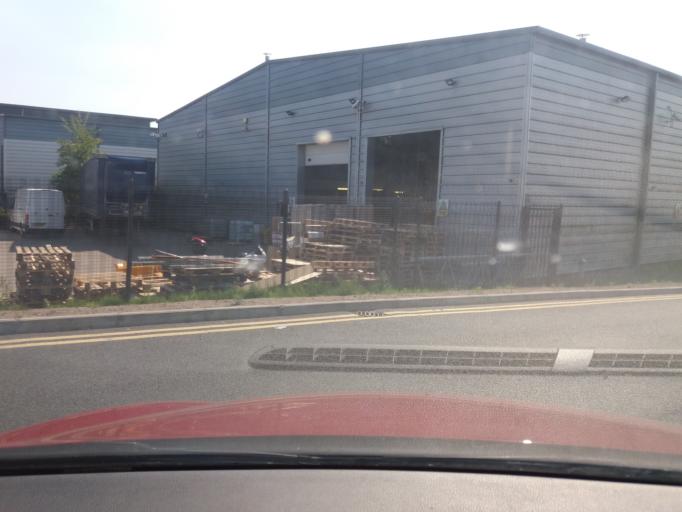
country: GB
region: England
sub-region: Lancashire
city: Clayton-le-Woods
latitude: 53.6863
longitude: -2.6677
